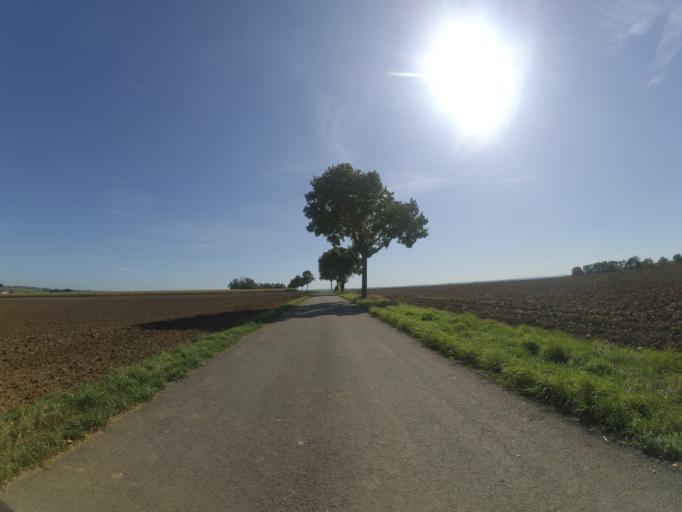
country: DE
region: Baden-Wuerttemberg
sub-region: Tuebingen Region
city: Nerenstetten
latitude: 48.5071
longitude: 10.0884
